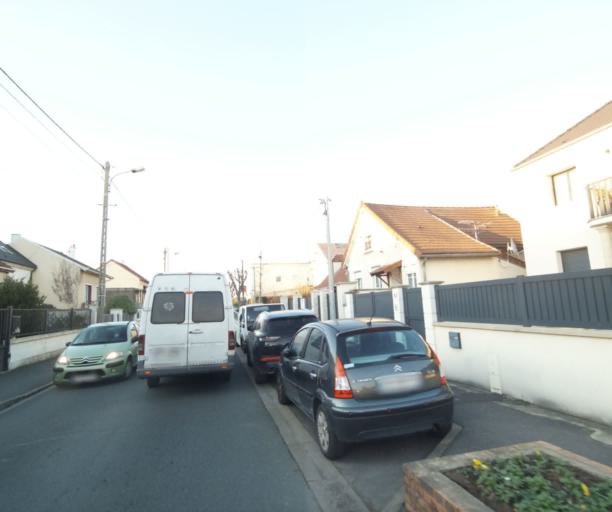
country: FR
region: Ile-de-France
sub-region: Departement du Val-d'Oise
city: Arnouville
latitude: 48.9868
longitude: 2.4239
